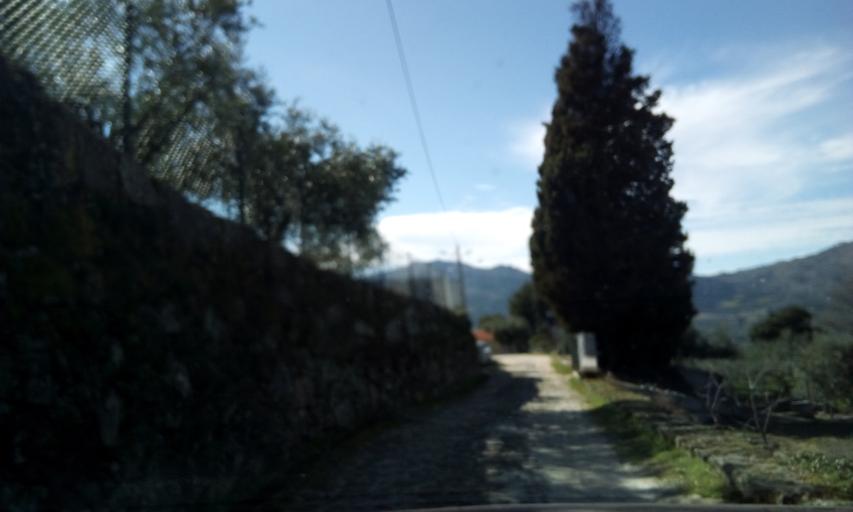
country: PT
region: Guarda
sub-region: Guarda
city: Guarda
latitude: 40.5846
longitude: -7.2897
